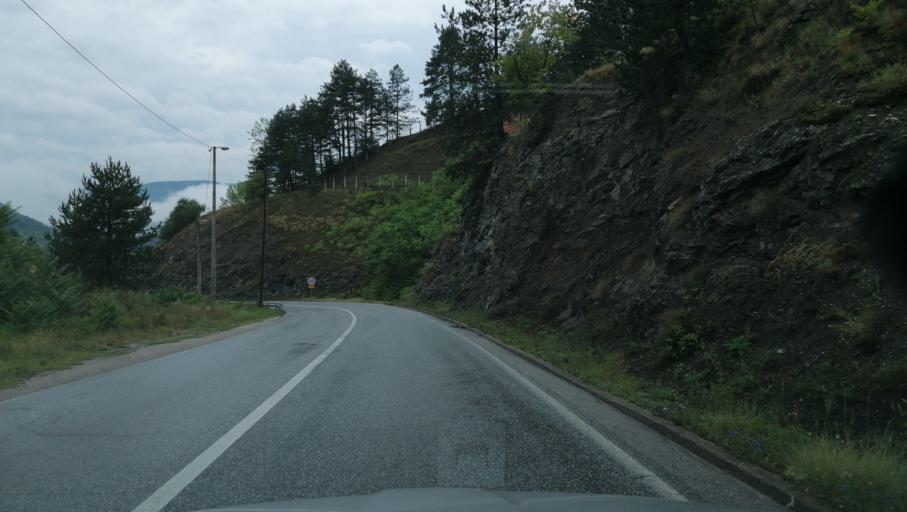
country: BA
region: Republika Srpska
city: Visegrad
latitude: 43.7829
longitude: 19.3026
